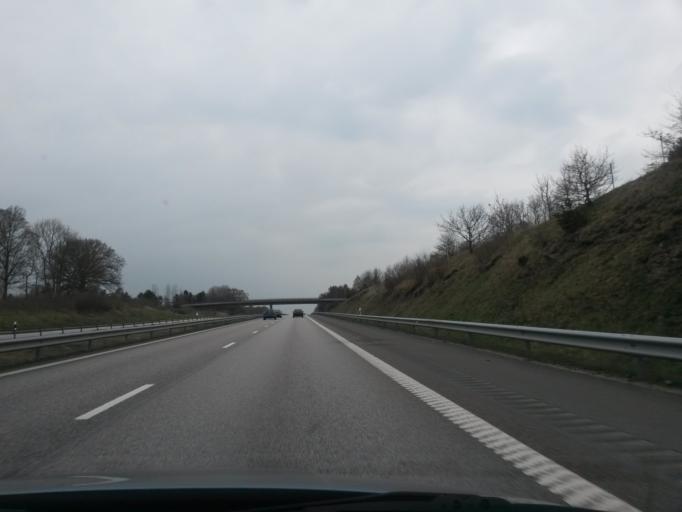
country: SE
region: Halland
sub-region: Kungsbacka Kommun
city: Frillesas
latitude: 57.2688
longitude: 12.2156
